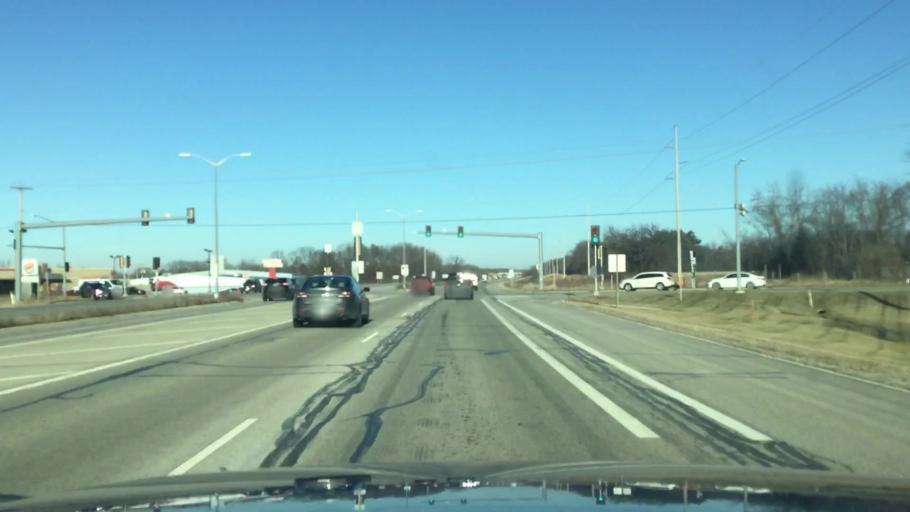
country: US
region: Wisconsin
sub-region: Racine County
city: Waterford
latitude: 42.7524
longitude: -88.2085
